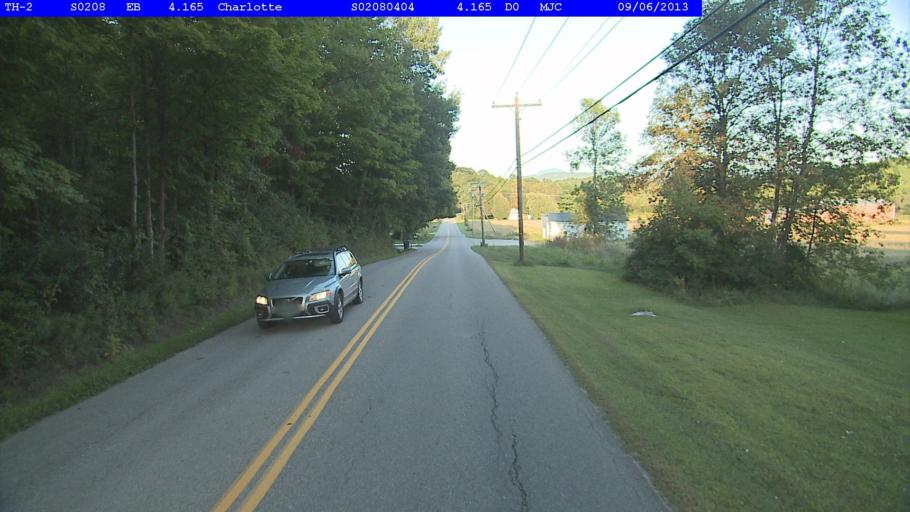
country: US
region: Vermont
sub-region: Chittenden County
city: Hinesburg
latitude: 44.3225
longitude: -73.1652
